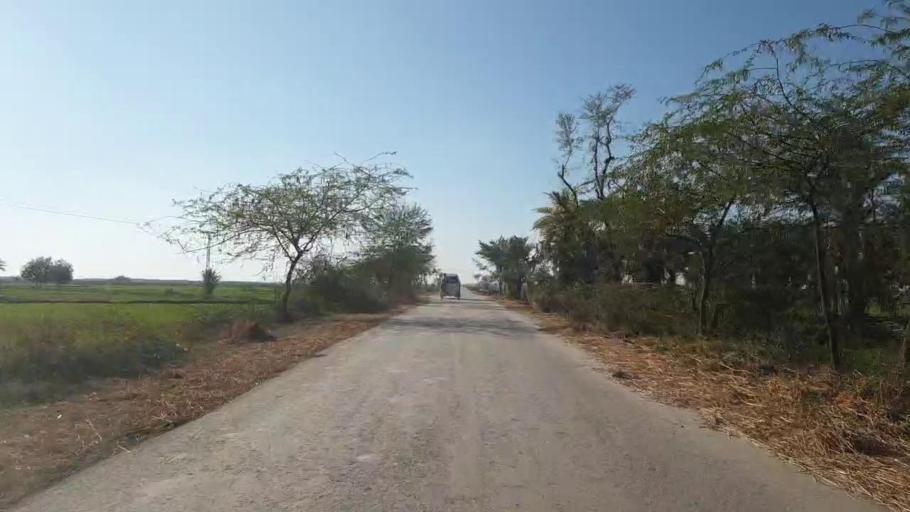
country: PK
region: Sindh
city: New Badah
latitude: 27.3244
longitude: 68.0690
